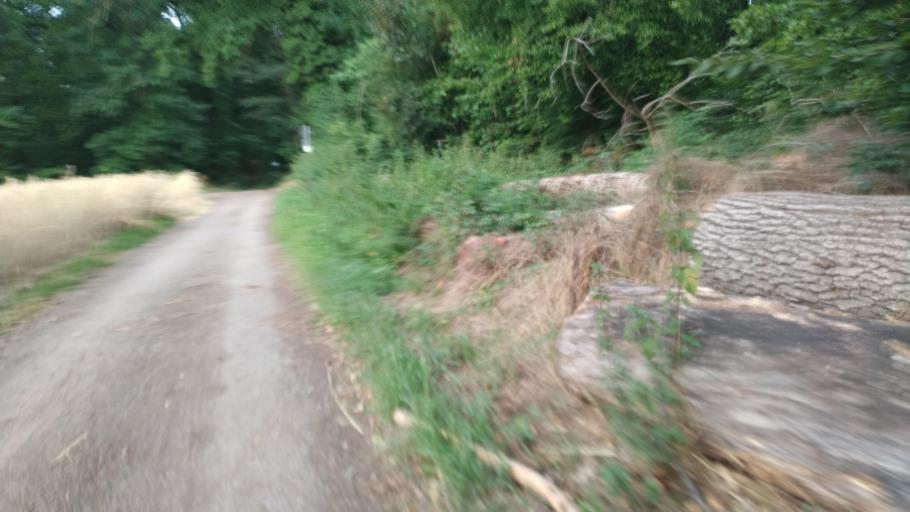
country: DE
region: Baden-Wuerttemberg
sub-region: Karlsruhe Region
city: Weingarten
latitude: 49.0791
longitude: 8.5374
